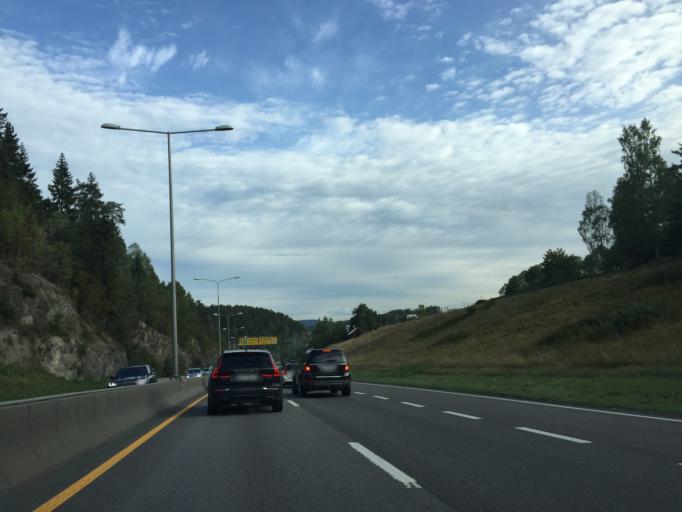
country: NO
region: Akershus
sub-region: Oppegard
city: Kolbotn
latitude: 59.8555
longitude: 10.8327
